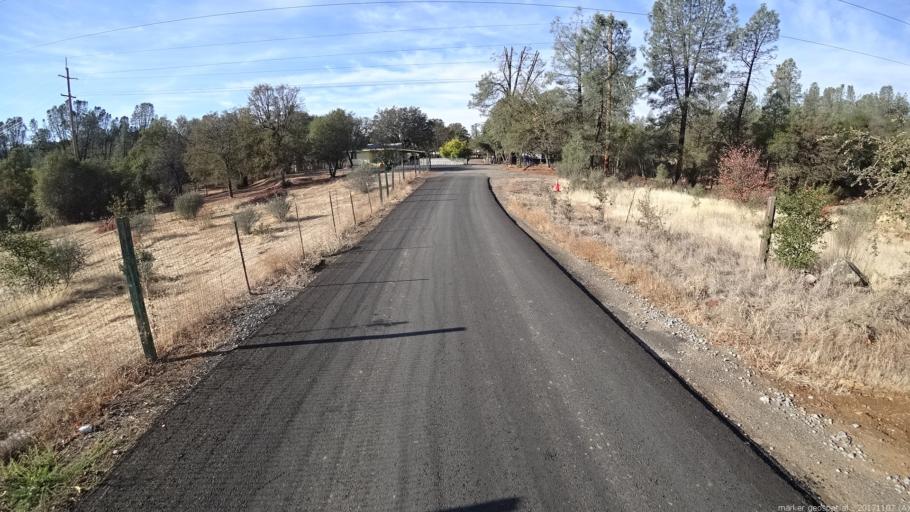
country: US
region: California
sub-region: Shasta County
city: Redding
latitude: 40.5468
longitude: -122.4310
